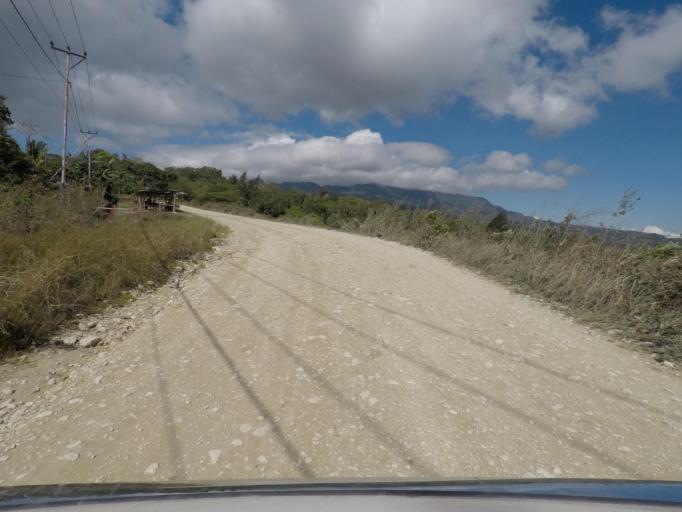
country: TL
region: Baucau
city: Venilale
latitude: -8.6789
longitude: 126.3724
